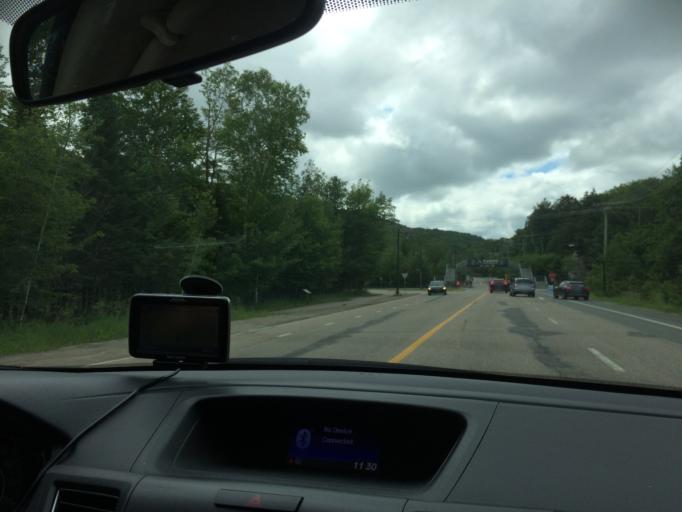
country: CA
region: Quebec
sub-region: Laurentides
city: Mont-Tremblant
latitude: 46.2064
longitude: -74.5876
